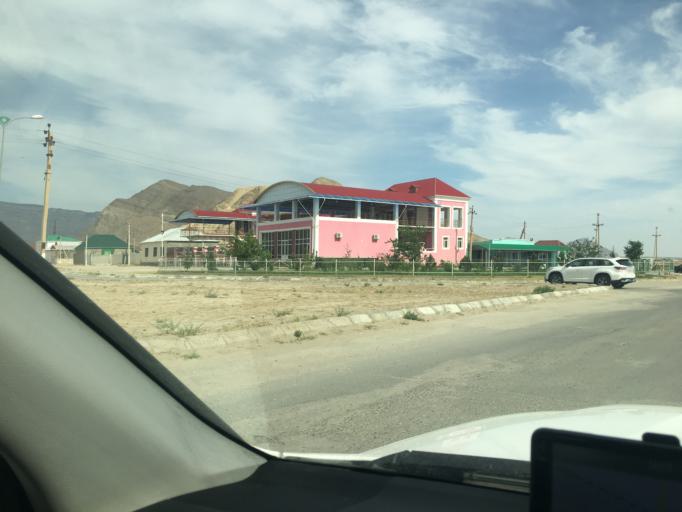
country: TM
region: Balkan
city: Balkanabat
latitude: 39.6233
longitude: 54.2434
